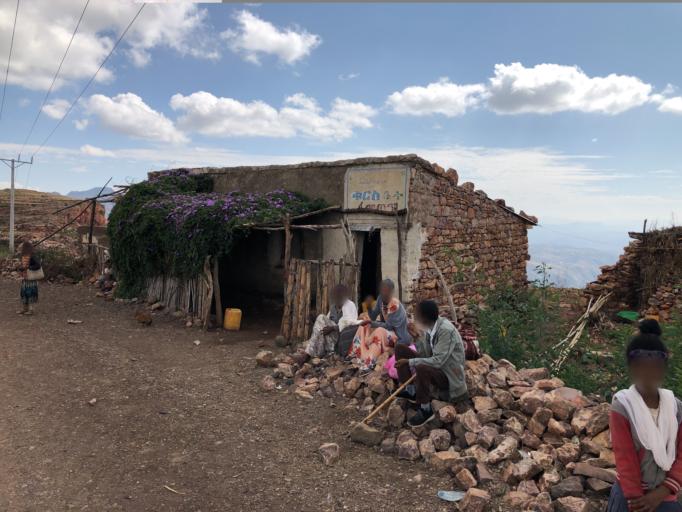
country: ET
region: Tigray
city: Adigrat
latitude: 14.1721
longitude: 39.3944
